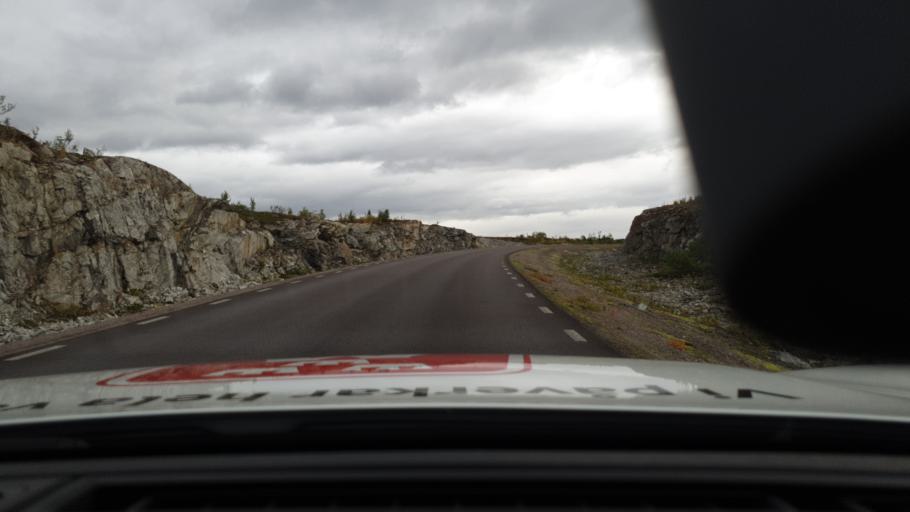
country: NO
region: Troms
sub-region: Bardu
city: Setermoen
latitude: 68.4300
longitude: 18.1956
